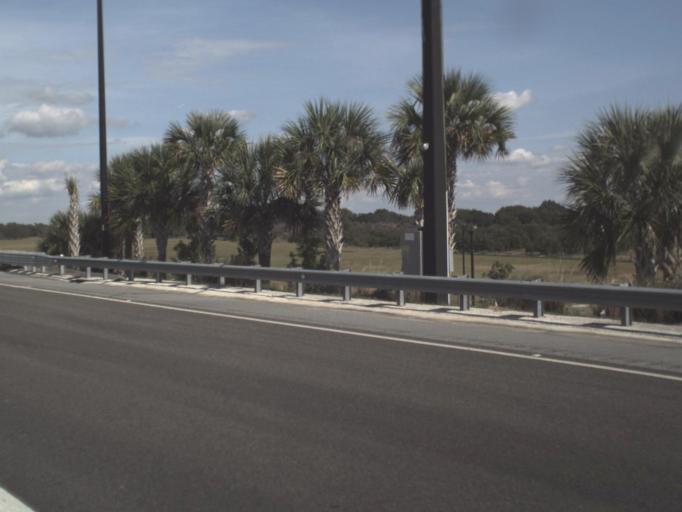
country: US
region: Florida
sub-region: Polk County
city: Polk City
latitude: 28.1351
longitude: -81.8399
